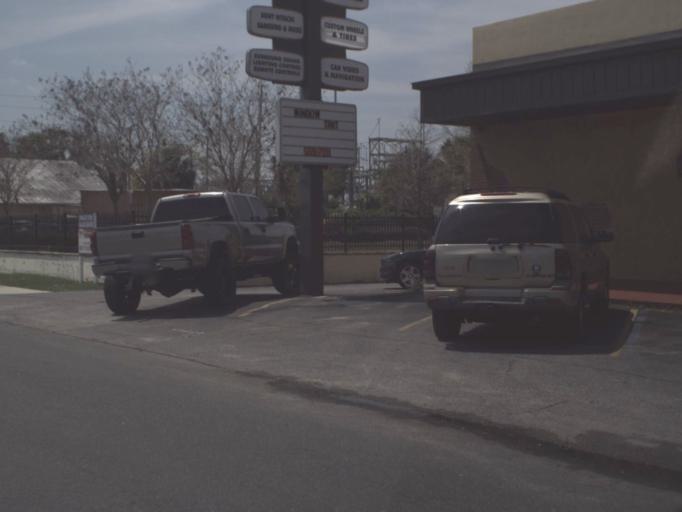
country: US
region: Florida
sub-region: Lake County
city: Eustis
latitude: 28.8512
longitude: -81.6857
